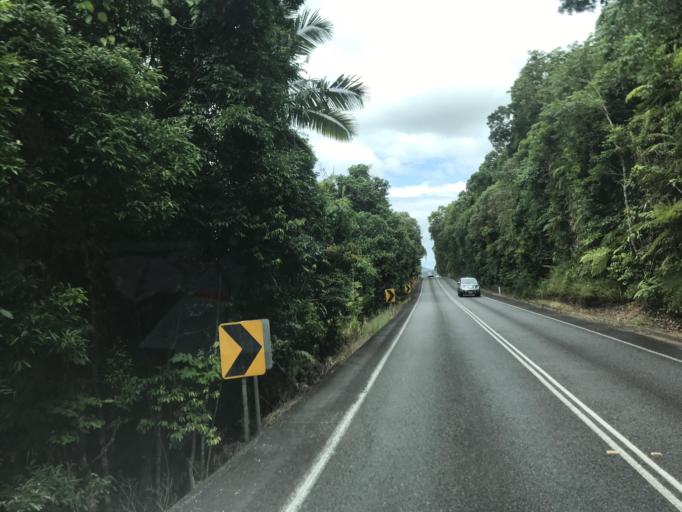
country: AU
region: Queensland
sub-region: Cassowary Coast
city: Innisfail
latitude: -17.8511
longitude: 146.0617
